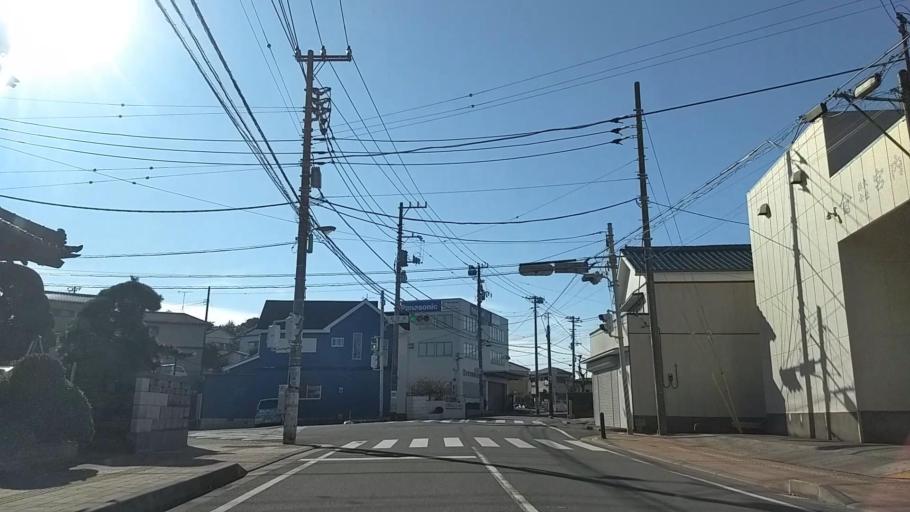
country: JP
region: Chiba
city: Hasaki
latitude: 35.7281
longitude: 140.8405
